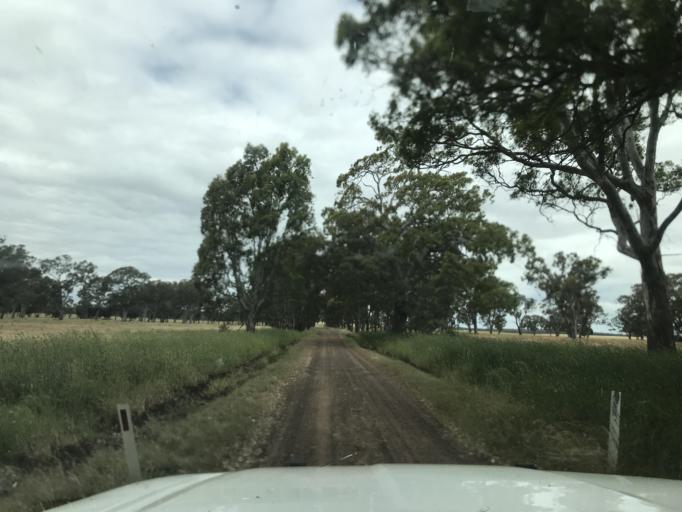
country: AU
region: South Australia
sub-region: Naracoorte and Lucindale
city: Naracoorte
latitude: -36.9252
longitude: 141.3098
